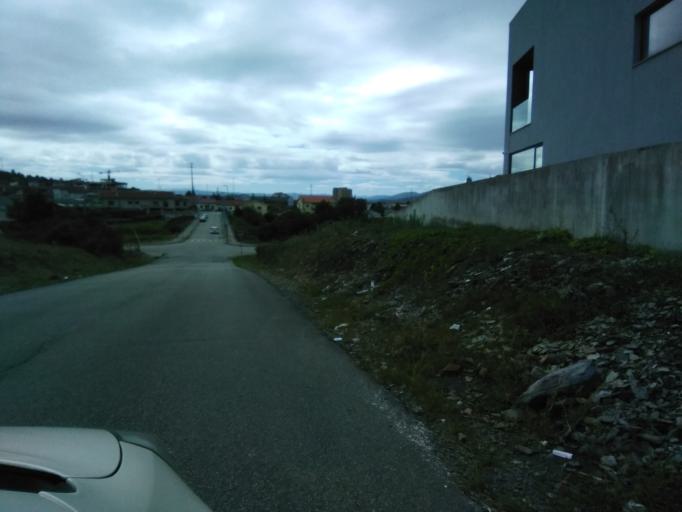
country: PT
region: Porto
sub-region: Valongo
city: Valongo
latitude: 41.1901
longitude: -8.4911
